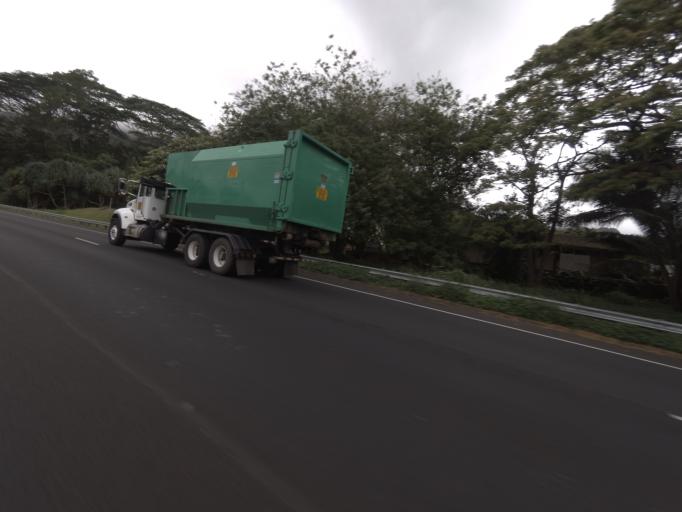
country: US
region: Hawaii
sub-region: Honolulu County
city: Kane'ohe
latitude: 21.4003
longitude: -157.8099
